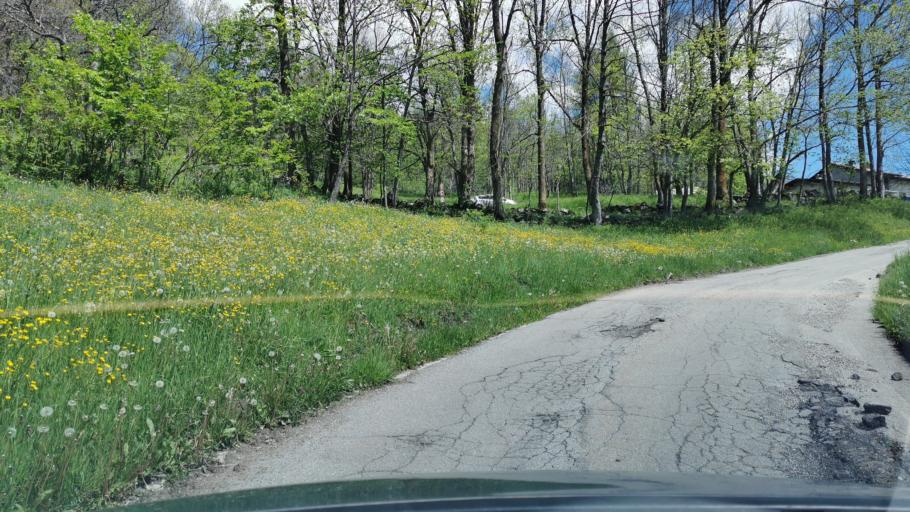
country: IT
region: Piedmont
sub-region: Provincia di Torino
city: Usseglio
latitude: 45.2194
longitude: 7.1887
